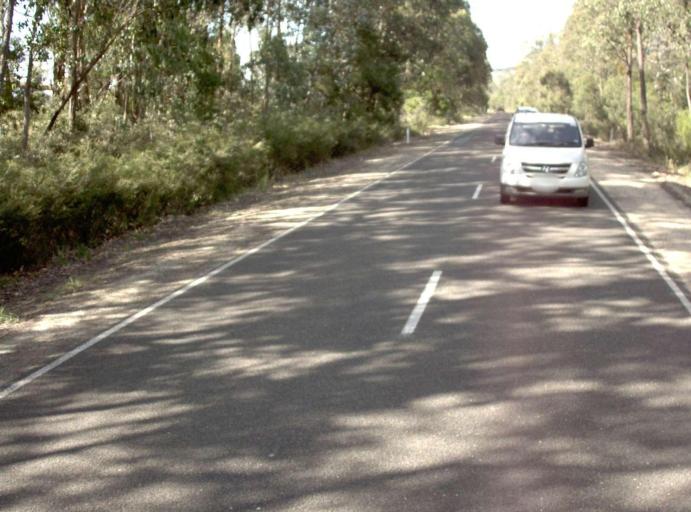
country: AU
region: Victoria
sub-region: East Gippsland
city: Lakes Entrance
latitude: -37.5674
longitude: 148.1322
